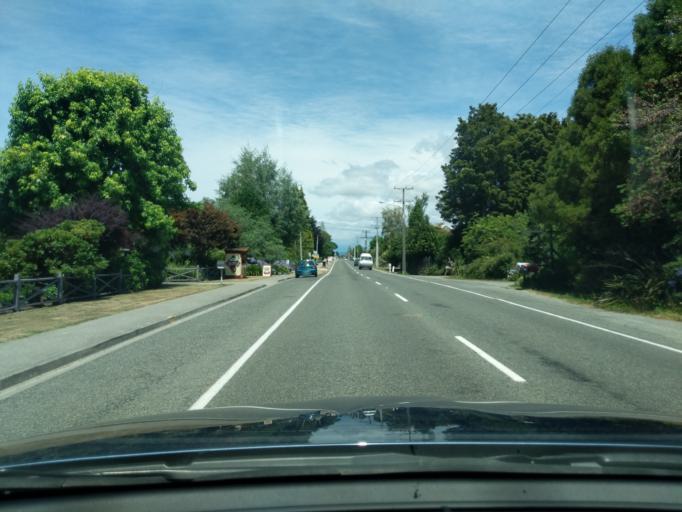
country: NZ
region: Tasman
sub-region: Tasman District
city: Motueka
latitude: -41.0830
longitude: 172.9971
